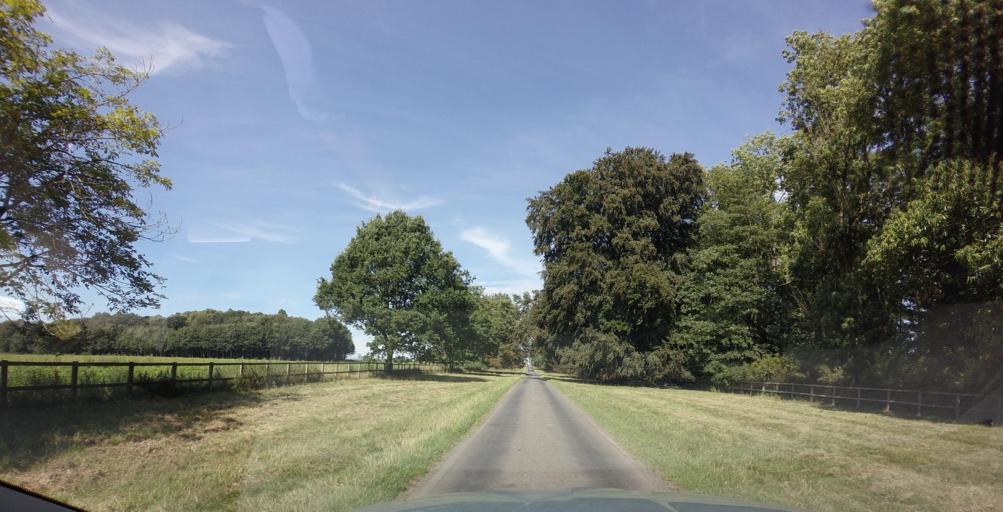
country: GB
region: England
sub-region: North Yorkshire
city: Ripon
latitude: 54.1085
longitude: -1.4714
